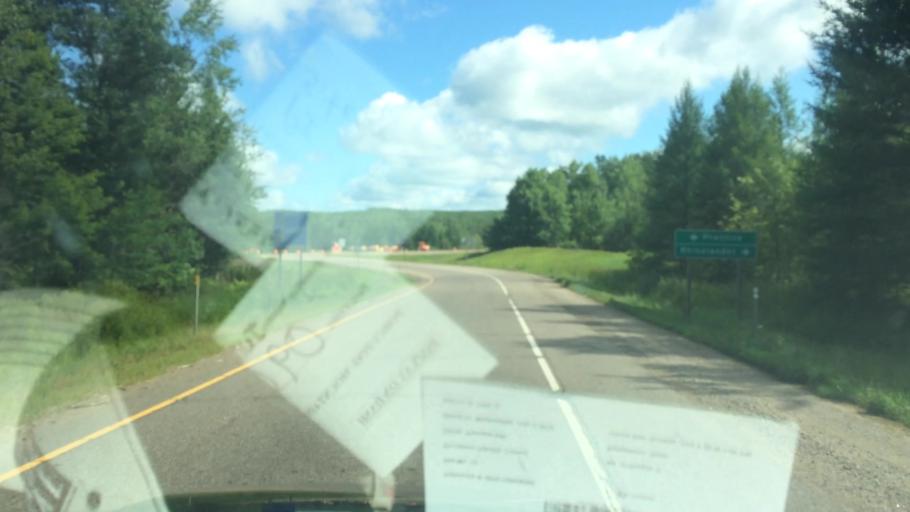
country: US
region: Wisconsin
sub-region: Lincoln County
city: Tomahawk
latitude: 45.5421
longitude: -89.6703
